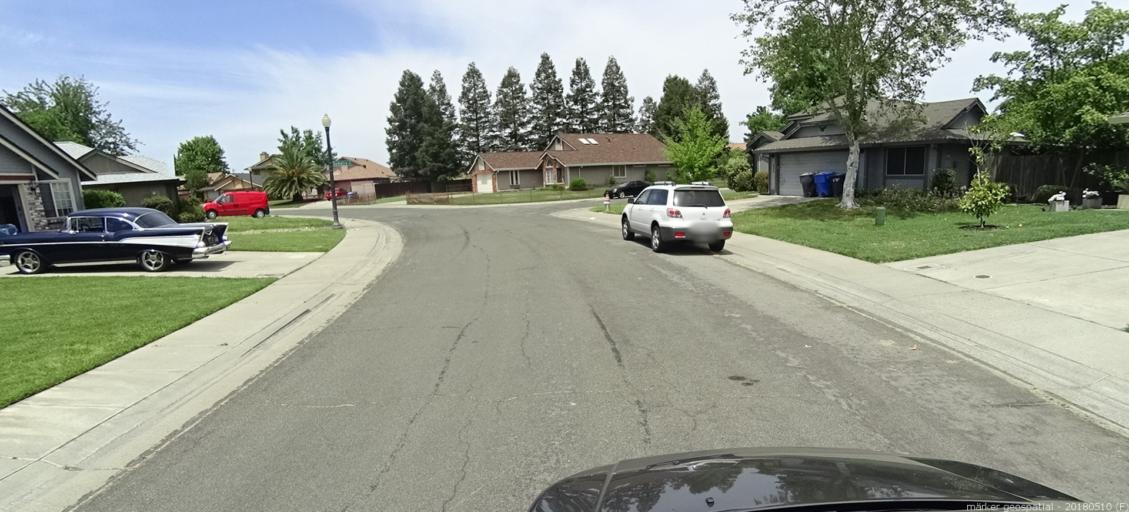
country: US
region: California
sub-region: Sacramento County
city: Rio Linda
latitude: 38.6585
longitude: -121.4636
